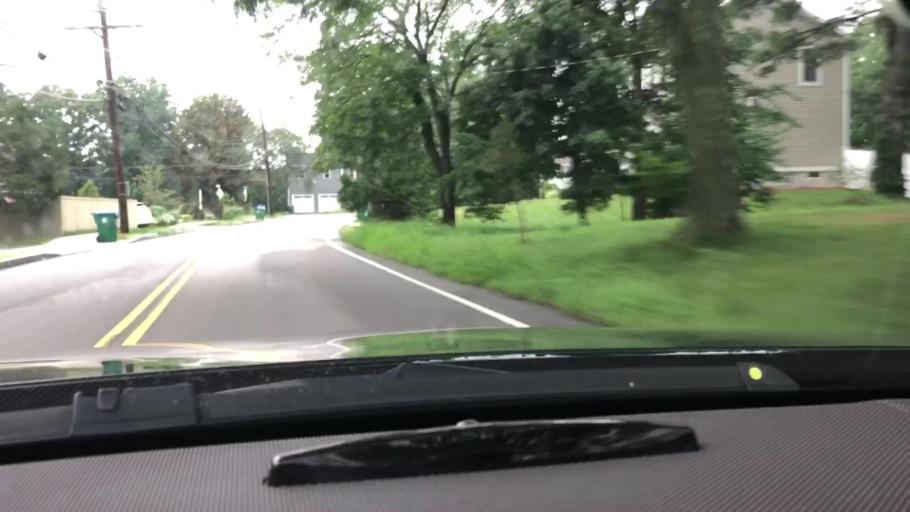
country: US
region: Massachusetts
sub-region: Norfolk County
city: Dedham
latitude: 42.2196
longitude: -71.1779
